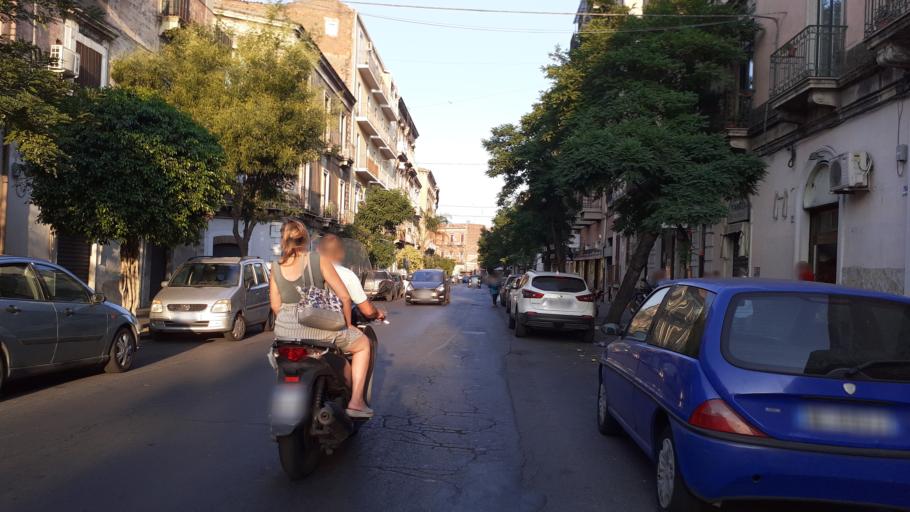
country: IT
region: Sicily
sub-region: Catania
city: Catania
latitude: 37.4981
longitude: 15.0824
